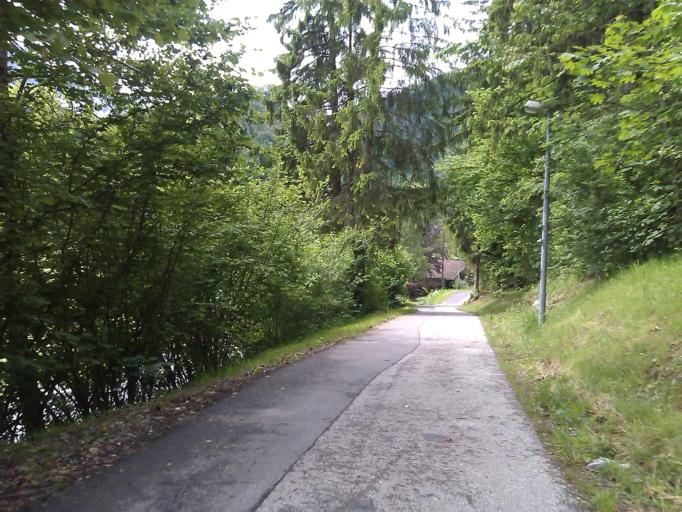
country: AT
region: Tyrol
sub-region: Politischer Bezirk Reutte
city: Reutte
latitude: 47.4745
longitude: 10.7226
